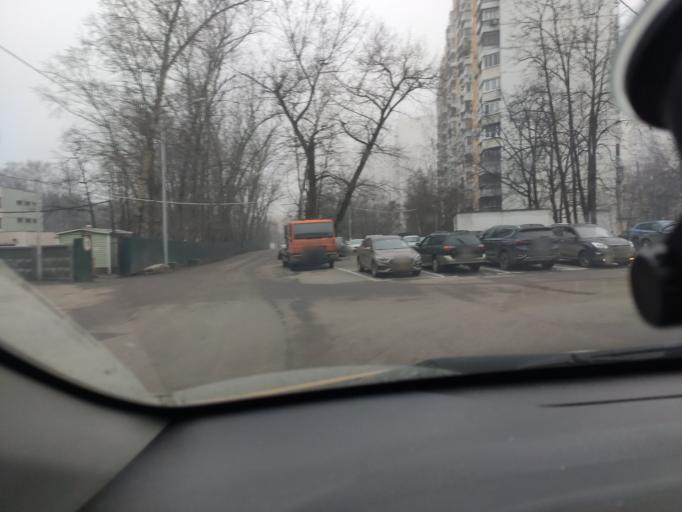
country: RU
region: Moscow
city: Chertanovo Yuzhnoye
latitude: 55.5899
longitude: 37.5947
